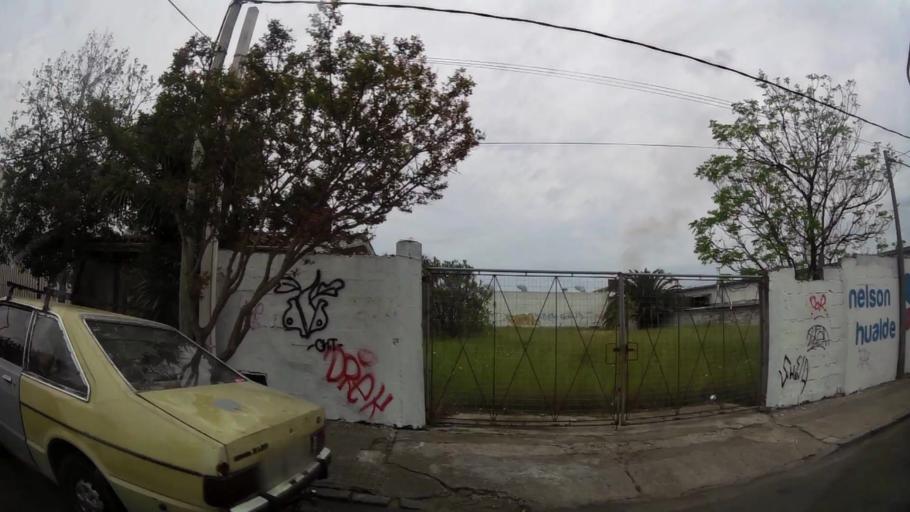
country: UY
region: Maldonado
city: Maldonado
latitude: -34.9078
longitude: -54.9544
